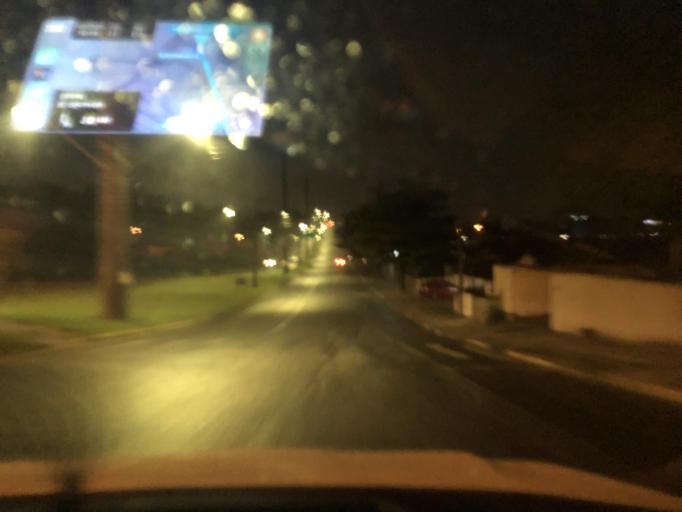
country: BR
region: Santa Catarina
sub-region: Joinville
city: Joinville
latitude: -26.3692
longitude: -48.8327
